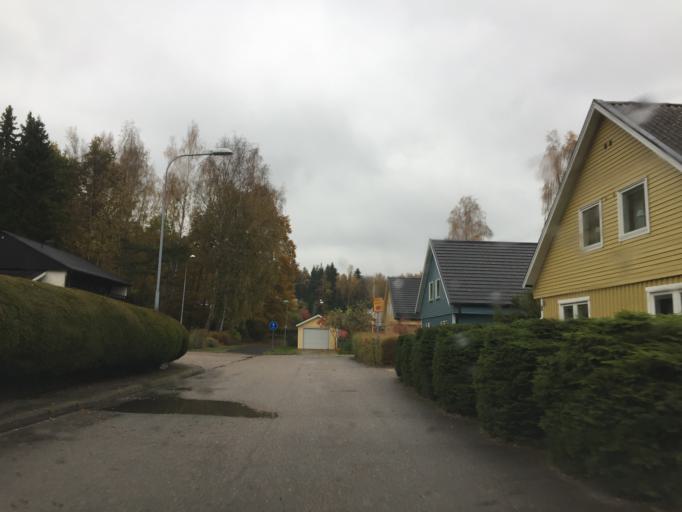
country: SE
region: Vaestra Goetaland
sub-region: Trollhattan
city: Trollhattan
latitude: 58.2872
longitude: 12.2594
